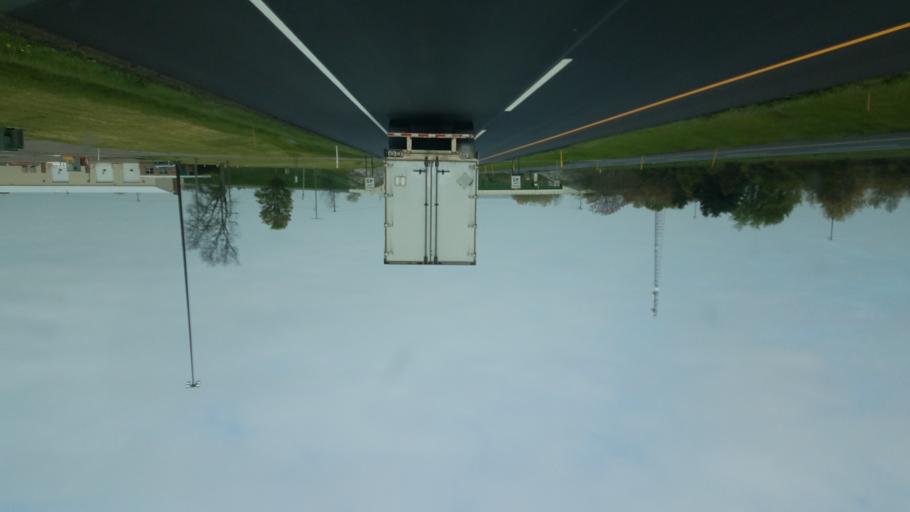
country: US
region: Indiana
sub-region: Saint Joseph County
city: Granger
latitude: 41.7314
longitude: -86.0594
